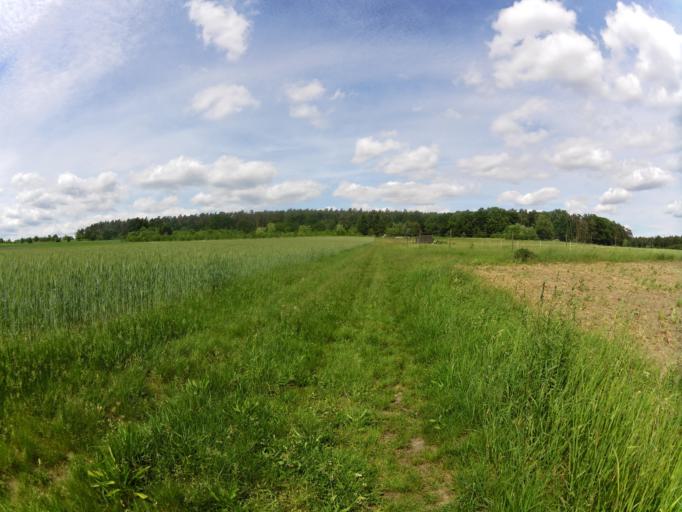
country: DE
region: Bavaria
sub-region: Regierungsbezirk Unterfranken
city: Sommerhausen
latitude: 49.6987
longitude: 10.0462
